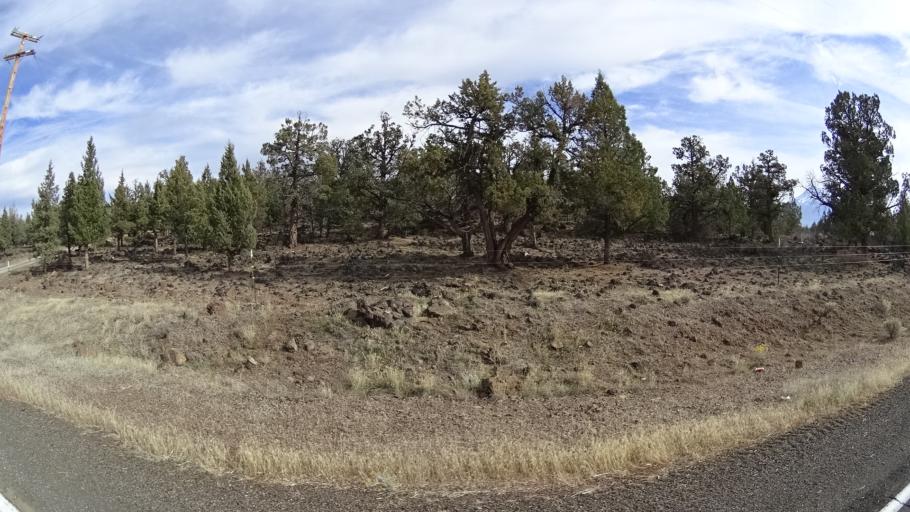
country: US
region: California
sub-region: Siskiyou County
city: Weed
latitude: 41.5988
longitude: -122.3954
